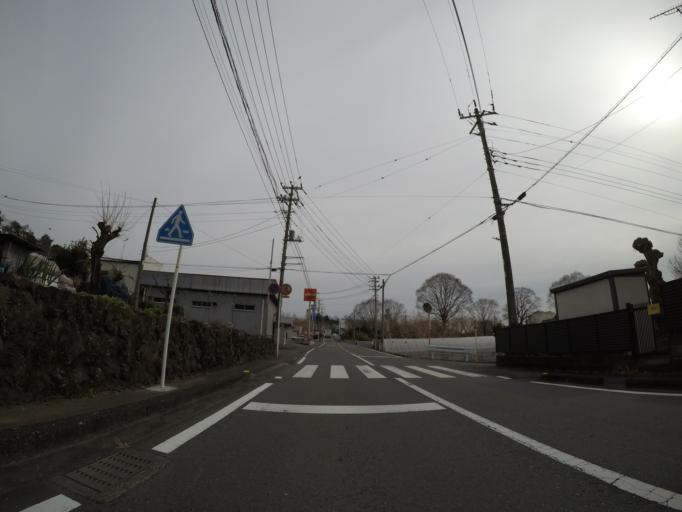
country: JP
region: Shizuoka
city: Fujinomiya
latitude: 35.2178
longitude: 138.6571
